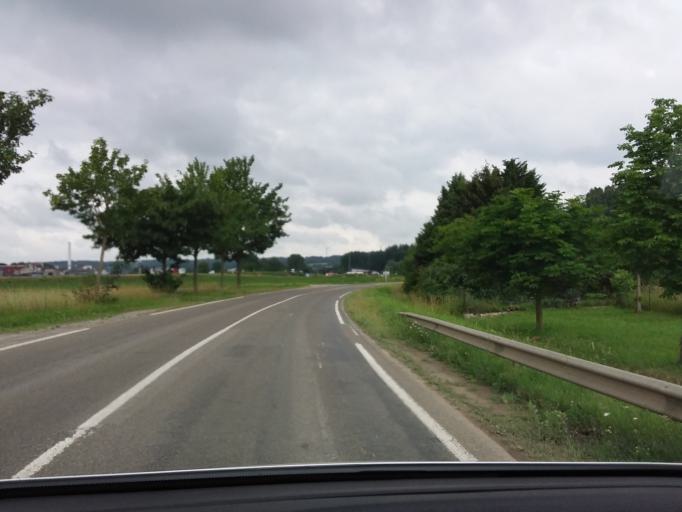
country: FR
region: Picardie
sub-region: Departement de l'Aisne
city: Bucy-le-Long
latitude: 49.3909
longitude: 3.3775
